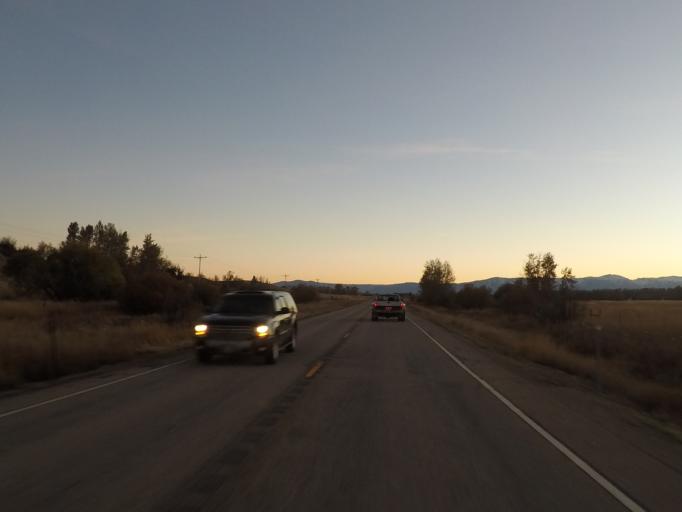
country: US
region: Montana
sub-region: Carbon County
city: Red Lodge
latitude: 45.4016
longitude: -109.1262
